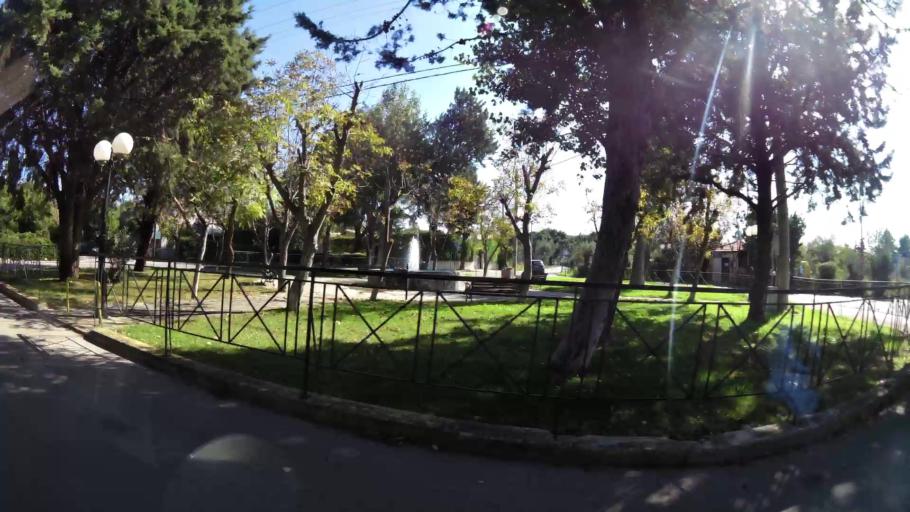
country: GR
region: Attica
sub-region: Nomarchia Athinas
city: Lykovrysi
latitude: 38.0829
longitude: 23.7786
